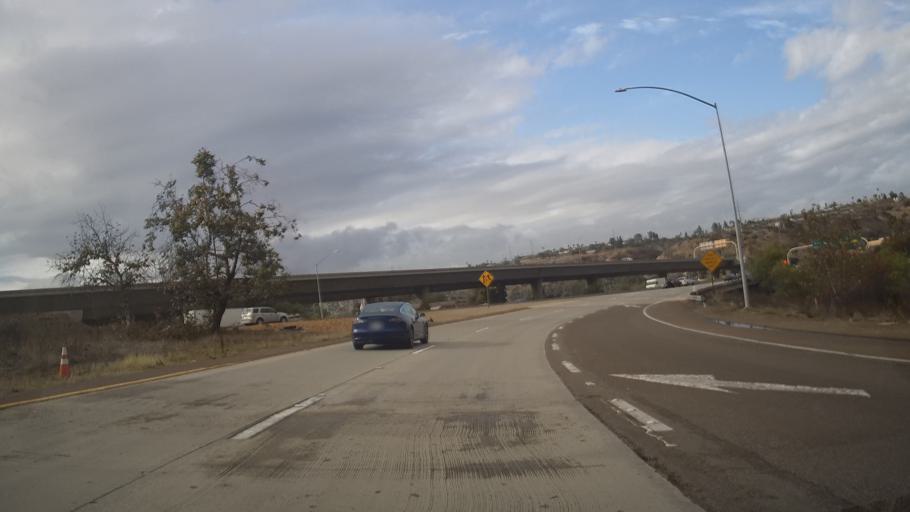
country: US
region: California
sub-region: San Diego County
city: San Diego
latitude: 32.7800
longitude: -117.1122
